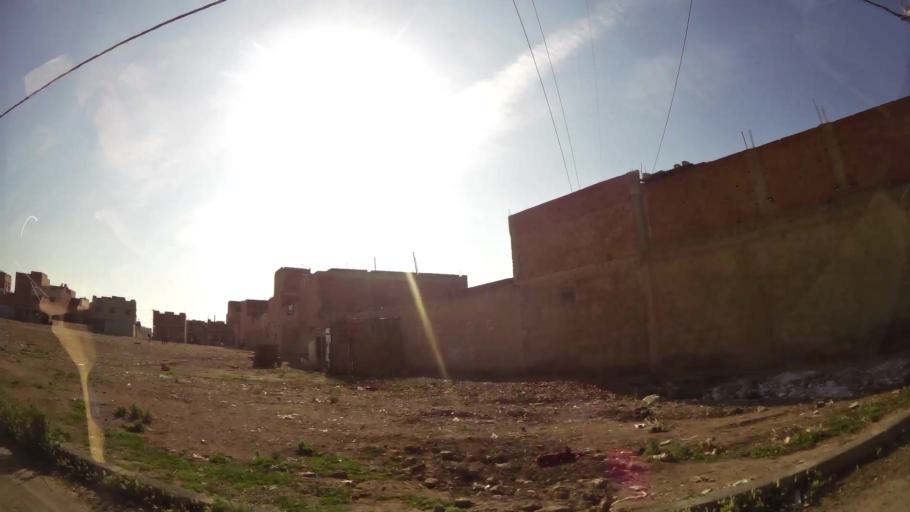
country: MA
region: Oriental
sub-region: Oujda-Angad
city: Oujda
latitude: 34.7256
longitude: -1.8905
